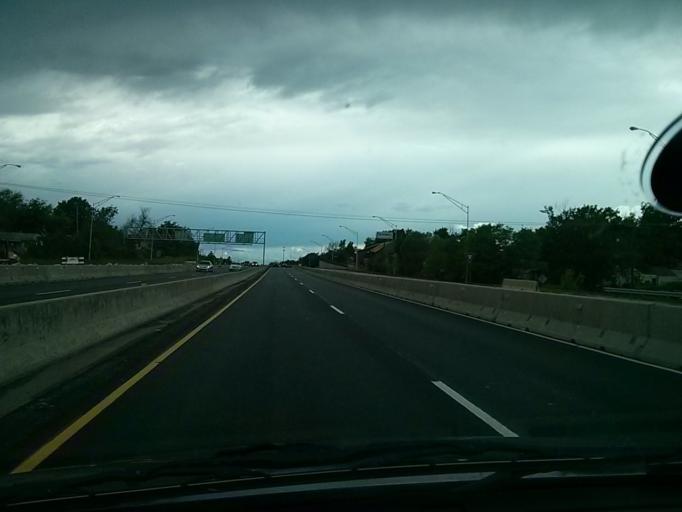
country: US
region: Oklahoma
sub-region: Tulsa County
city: Tulsa
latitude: 36.1593
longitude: -95.9246
